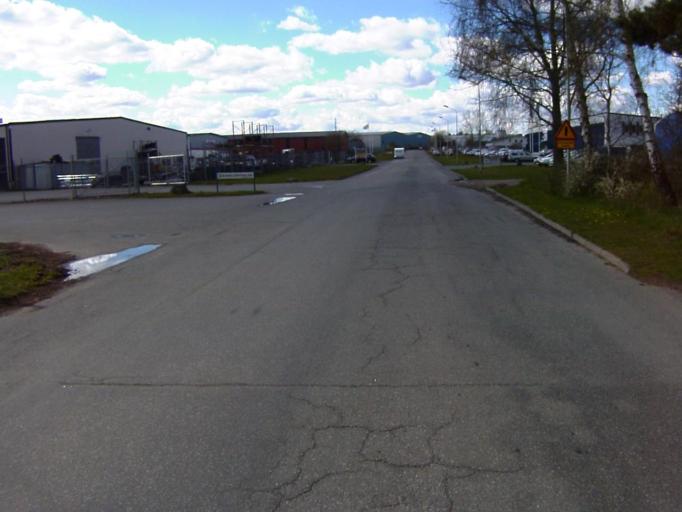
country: SE
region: Skane
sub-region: Kristianstads Kommun
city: Norra Asum
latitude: 56.0068
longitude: 14.1041
